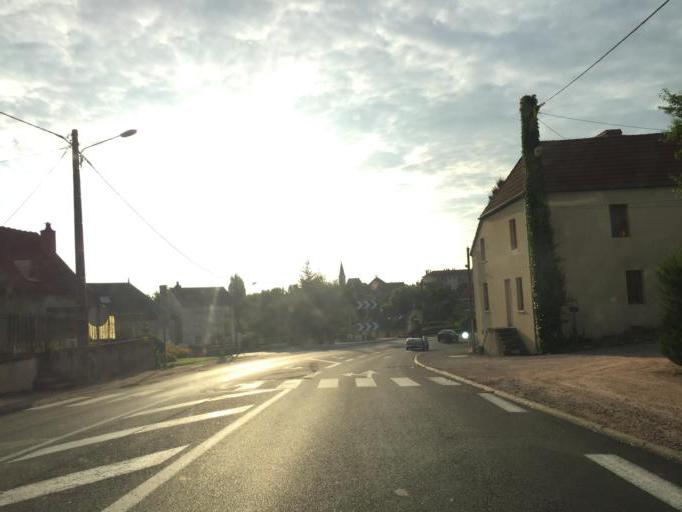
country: FR
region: Auvergne
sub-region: Departement de l'Allier
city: Varennes-sur-Allier
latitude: 46.3101
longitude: 3.4081
